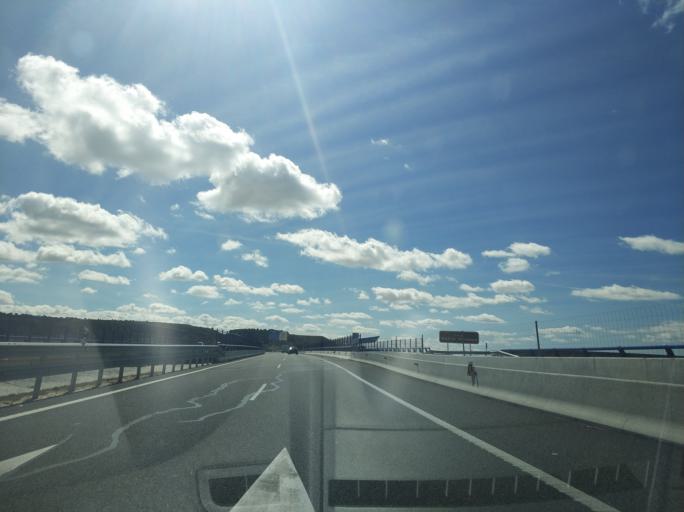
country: ES
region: Castille and Leon
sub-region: Provincia de Valladolid
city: Santovenia de Pisuerga
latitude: 41.7052
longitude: -4.6732
